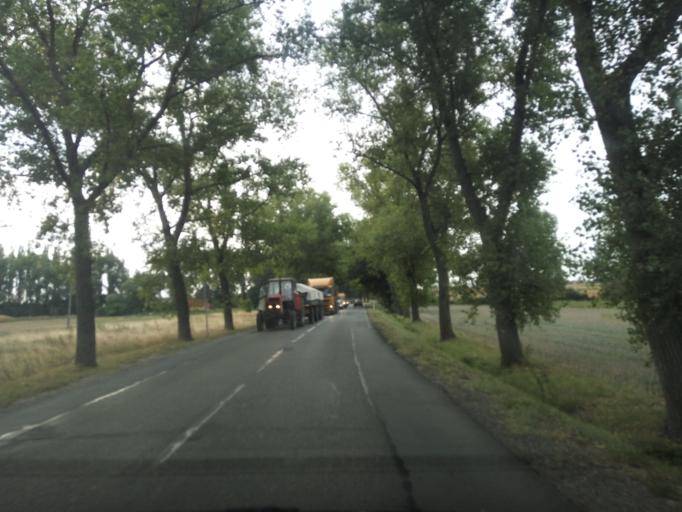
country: PL
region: Lower Silesian Voivodeship
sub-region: Powiat strzelinski
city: Strzelin
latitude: 50.8081
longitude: 17.0607
